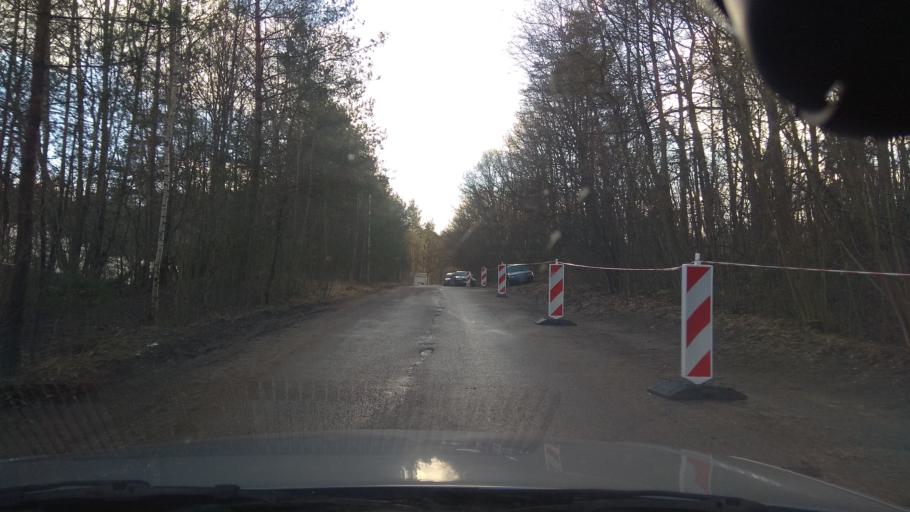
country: LT
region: Vilnius County
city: Lazdynai
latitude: 54.6432
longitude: 25.2225
